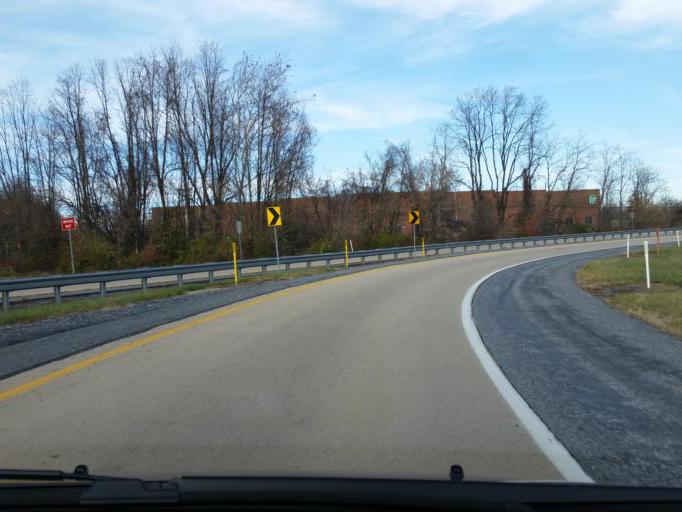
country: US
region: Pennsylvania
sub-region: Dauphin County
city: Highspire
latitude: 40.2263
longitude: -76.7614
